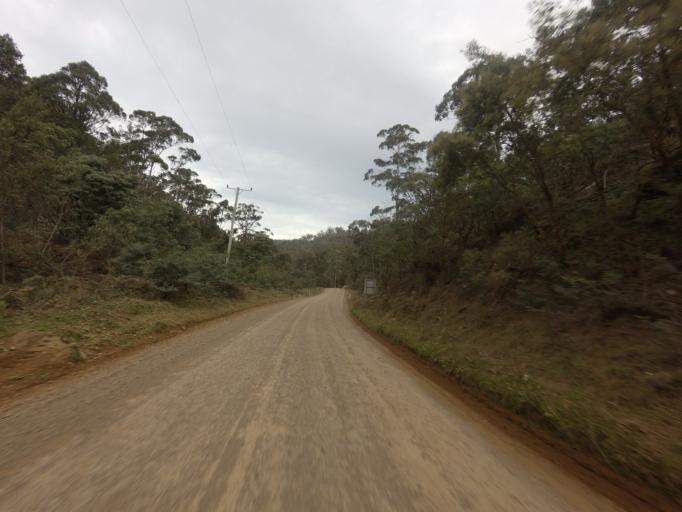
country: AU
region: Tasmania
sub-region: Derwent Valley
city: New Norfolk
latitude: -42.5892
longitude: 147.0257
